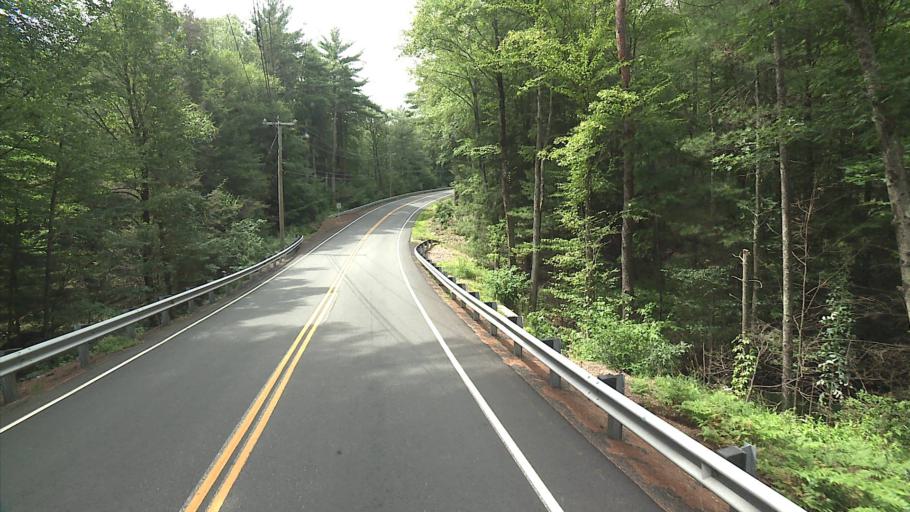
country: US
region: Massachusetts
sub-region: Hampden County
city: Holland
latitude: 41.9935
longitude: -72.1457
